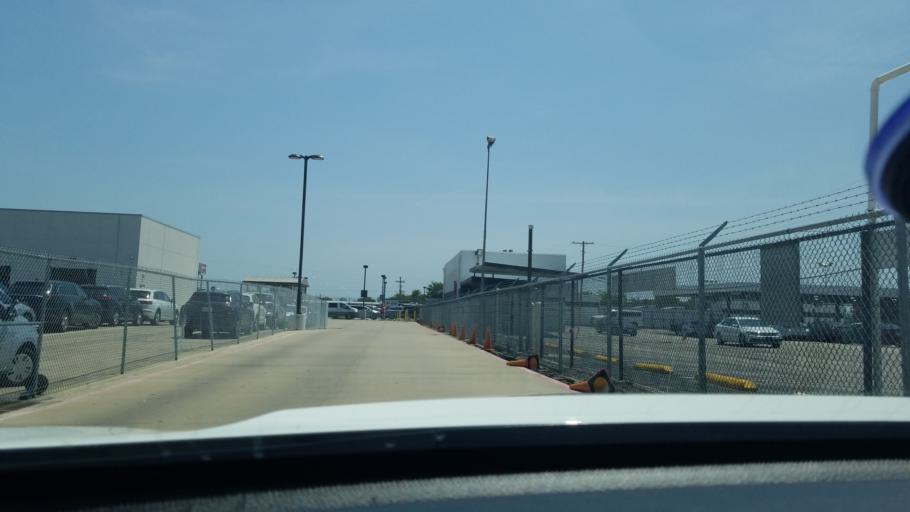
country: US
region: Texas
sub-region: Dallas County
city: University Park
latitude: 32.8384
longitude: -96.8426
